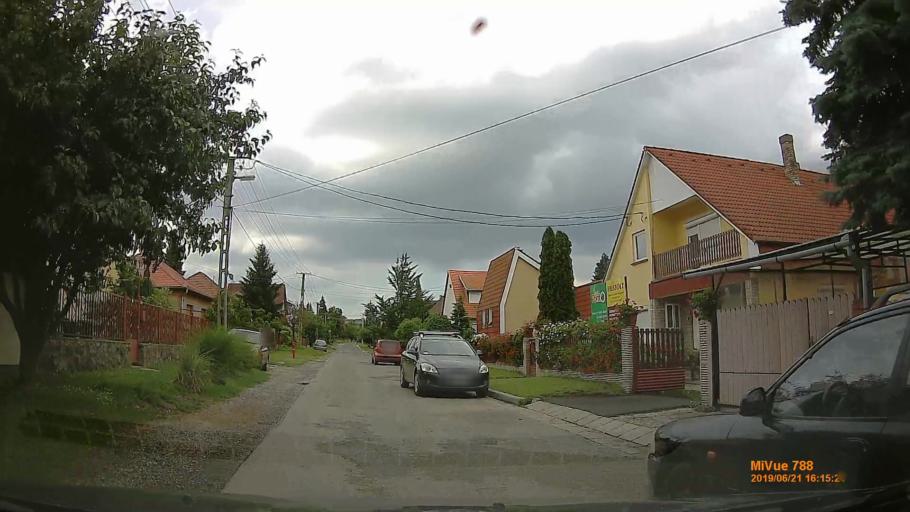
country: HU
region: Baranya
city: Pecs
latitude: 46.1022
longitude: 18.2695
